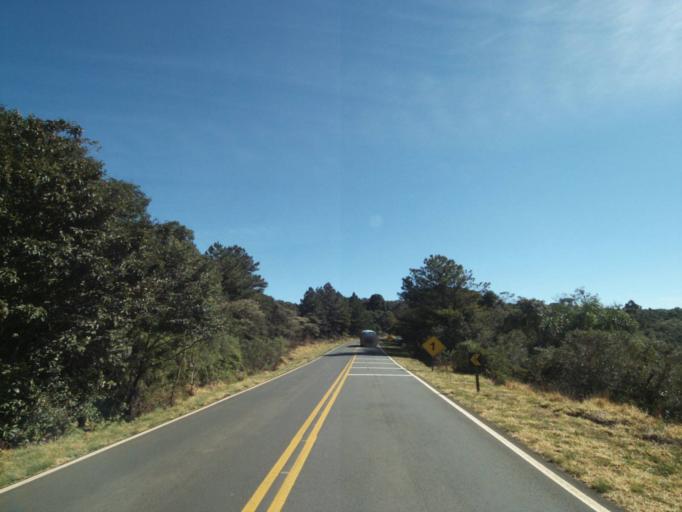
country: BR
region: Parana
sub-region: Castro
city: Castro
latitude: -24.7292
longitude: -50.1843
